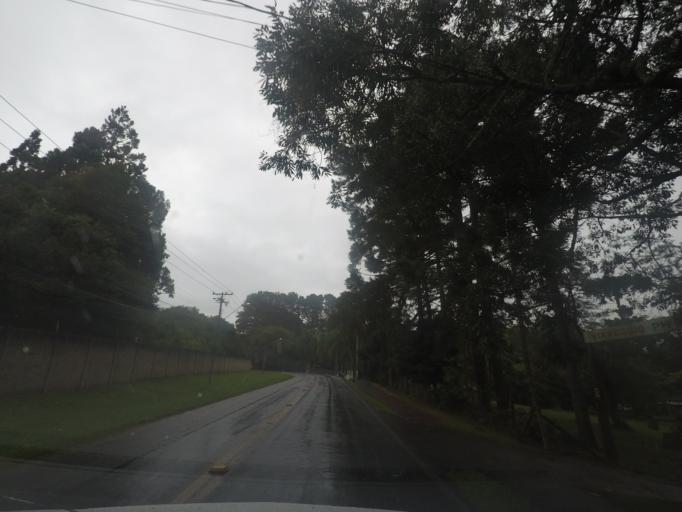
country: BR
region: Parana
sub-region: Quatro Barras
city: Quatro Barras
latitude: -25.3742
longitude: -49.1049
